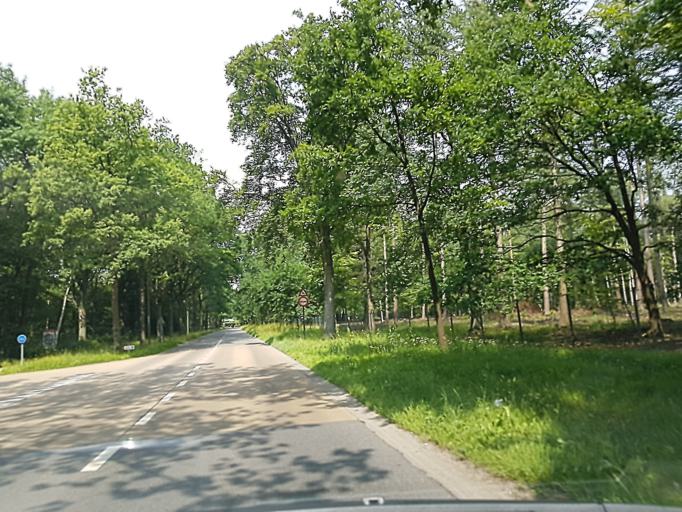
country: BE
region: Flanders
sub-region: Provincie Antwerpen
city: Wijnegem
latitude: 51.2433
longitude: 4.5395
